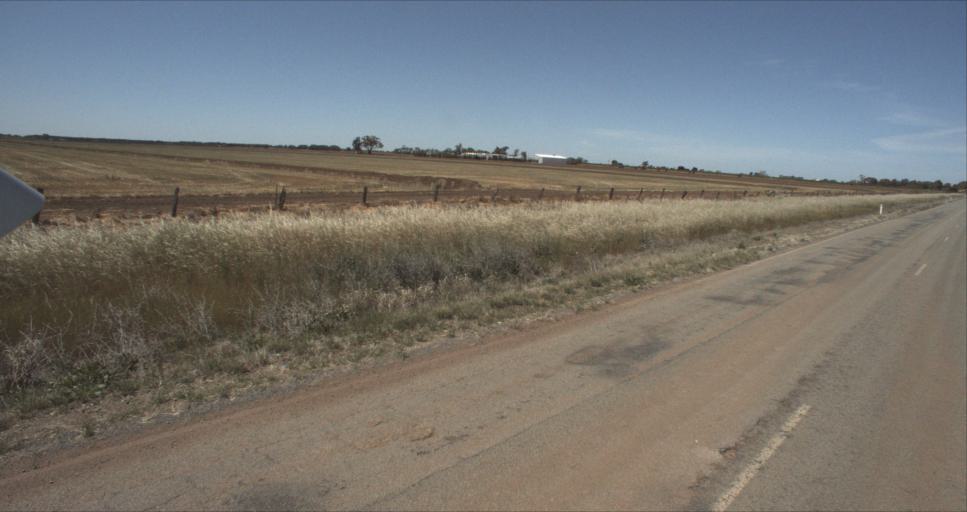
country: AU
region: New South Wales
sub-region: Leeton
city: Leeton
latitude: -34.5144
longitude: 146.2845
